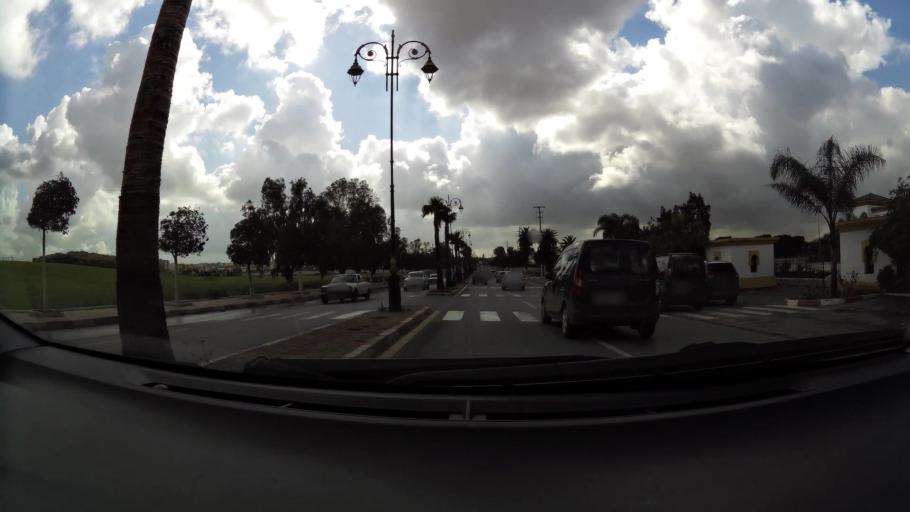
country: MA
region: Grand Casablanca
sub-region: Mediouna
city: Tit Mellil
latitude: 33.5604
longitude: -7.4915
